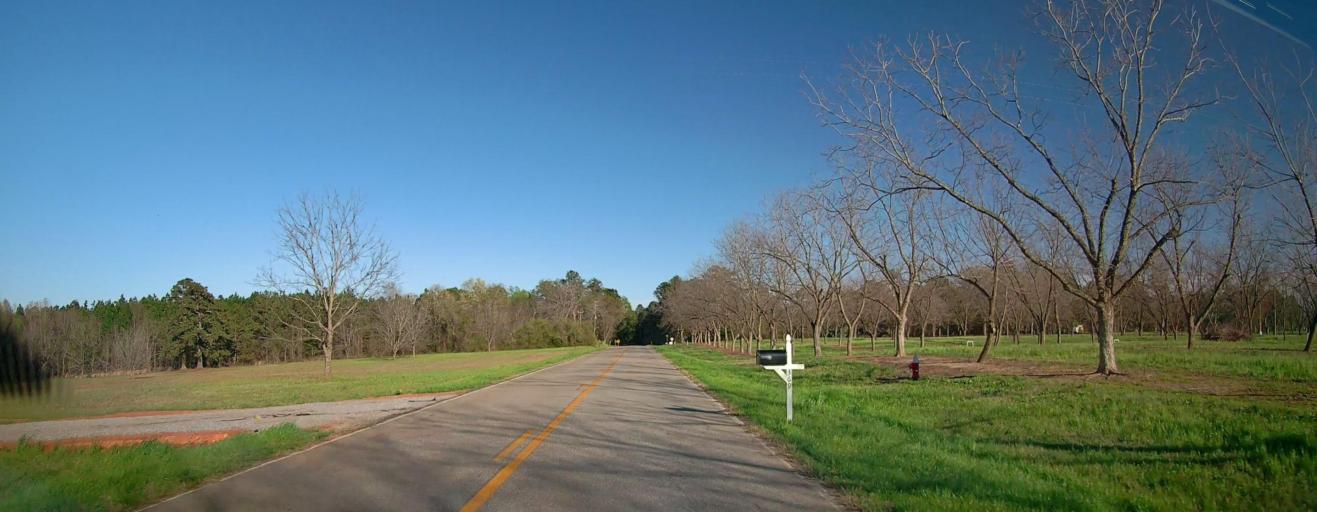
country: US
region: Georgia
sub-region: Houston County
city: Perry
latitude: 32.3651
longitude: -83.6743
